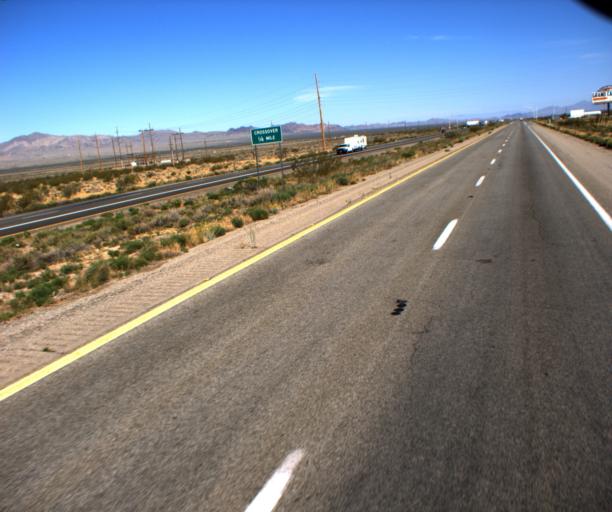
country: US
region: Arizona
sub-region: Mohave County
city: Dolan Springs
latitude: 35.5308
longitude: -114.3530
